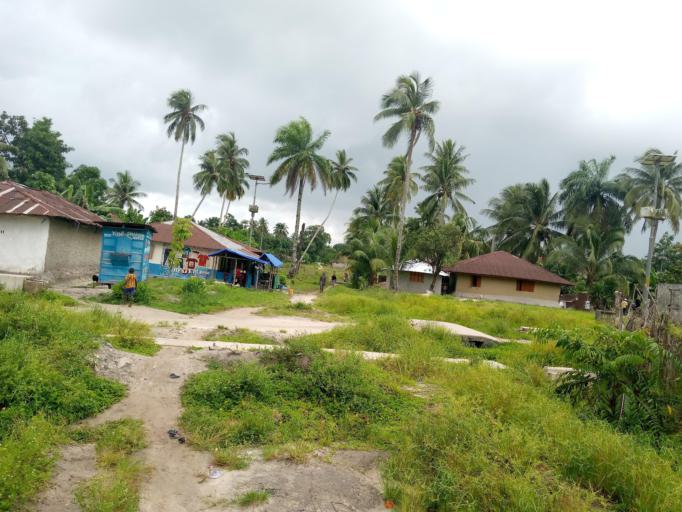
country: SL
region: Southern Province
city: Bonthe
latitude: 7.5283
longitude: -12.5047
